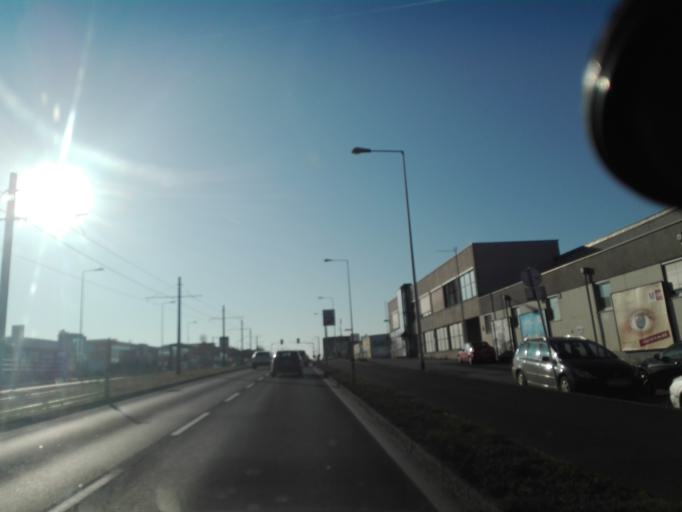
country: AT
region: Upper Austria
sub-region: Politischer Bezirk Linz-Land
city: Leonding
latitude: 48.2727
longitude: 14.2707
